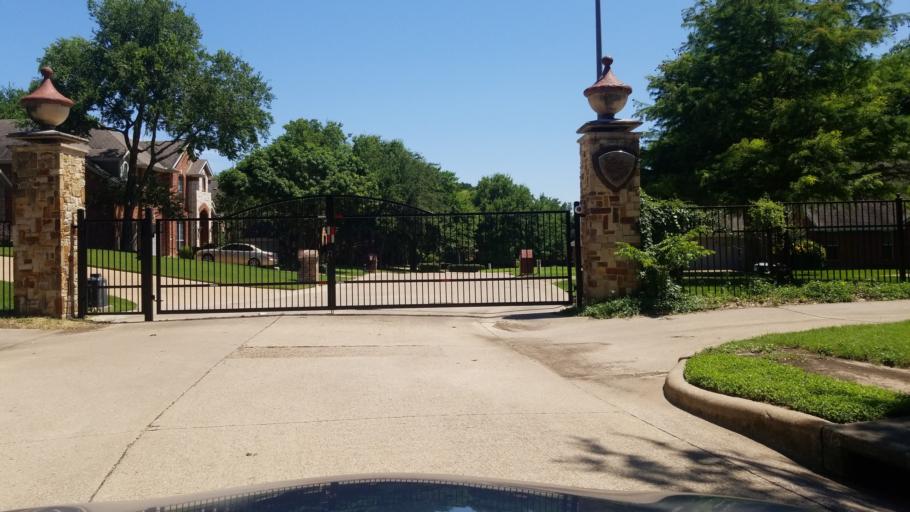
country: US
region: Texas
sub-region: Dallas County
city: Grand Prairie
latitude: 32.6844
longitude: -96.9988
